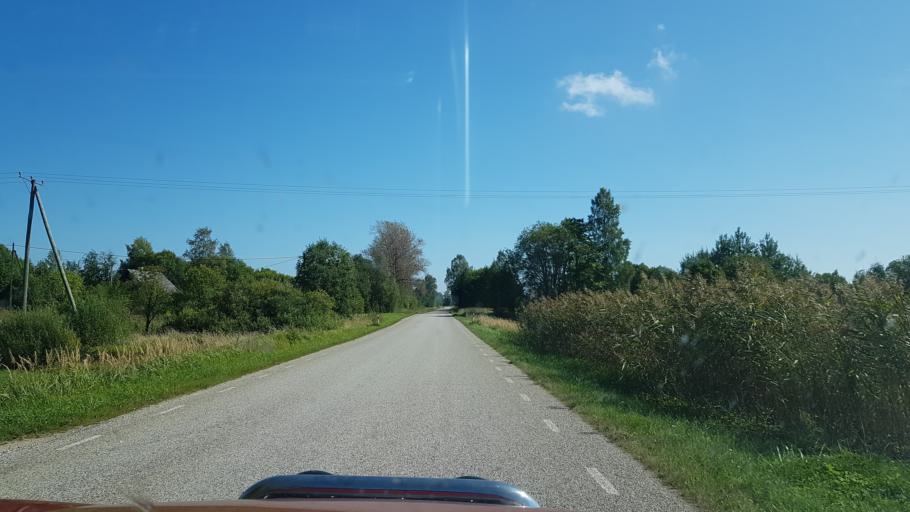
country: EE
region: Polvamaa
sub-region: Raepina vald
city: Rapina
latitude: 58.2294
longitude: 27.3839
